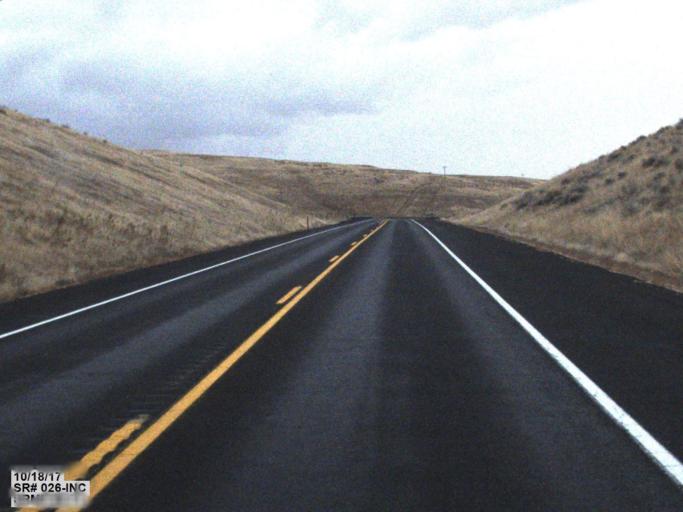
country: US
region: Washington
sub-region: Columbia County
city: Dayton
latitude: 46.7658
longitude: -118.0085
